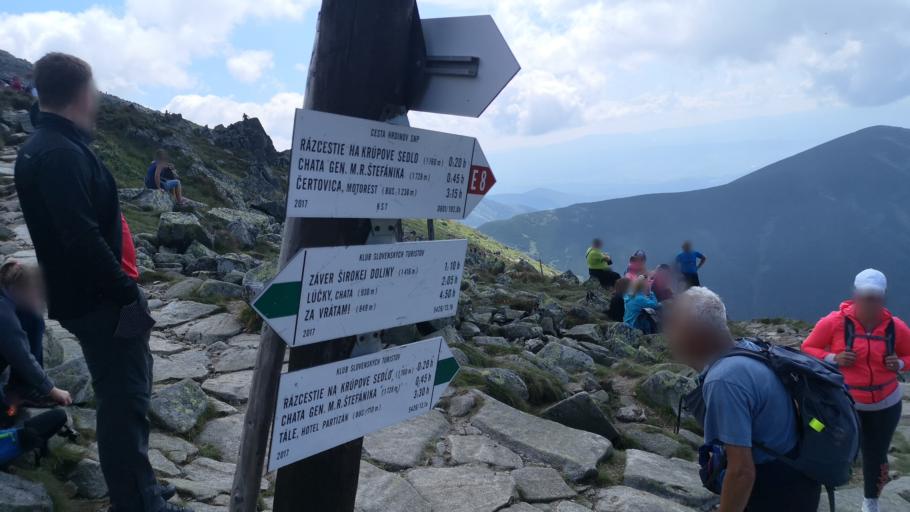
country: SK
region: Banskobystricky
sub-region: Okres Banska Bystrica
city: Brezno
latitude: 48.9390
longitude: 19.6301
